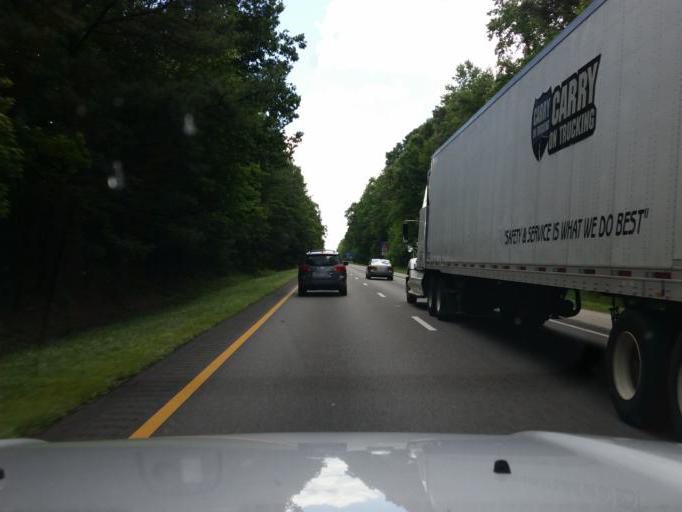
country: US
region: Virginia
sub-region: James City County
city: Williamsburg
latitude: 37.3634
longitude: -76.7437
